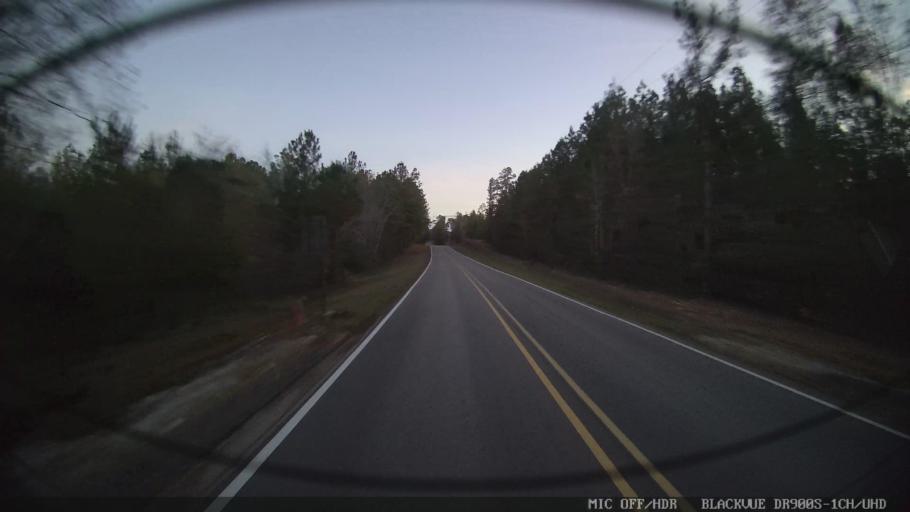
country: US
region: Mississippi
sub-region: Perry County
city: New Augusta
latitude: 31.0812
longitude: -89.1877
